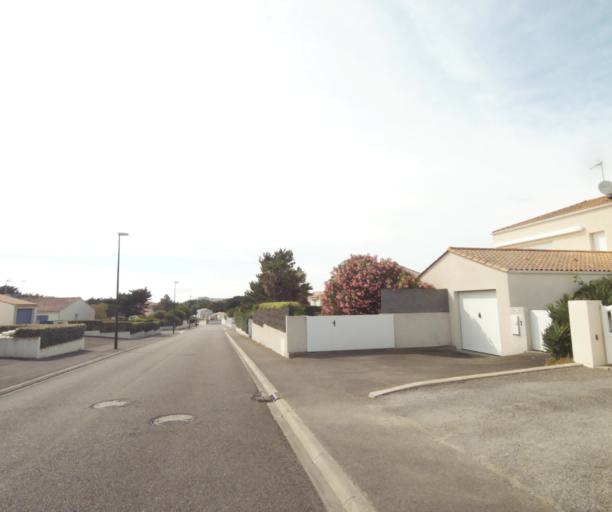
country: FR
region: Pays de la Loire
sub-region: Departement de la Vendee
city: Chateau-d'Olonne
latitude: 46.4816
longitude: -1.7545
